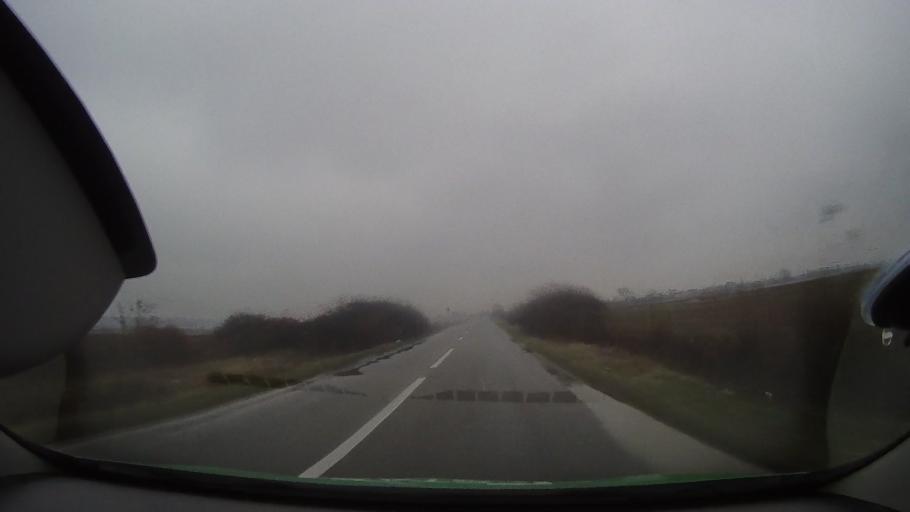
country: RO
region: Bihor
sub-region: Comuna Tinca
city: Gurbediu
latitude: 46.7901
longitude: 21.8469
